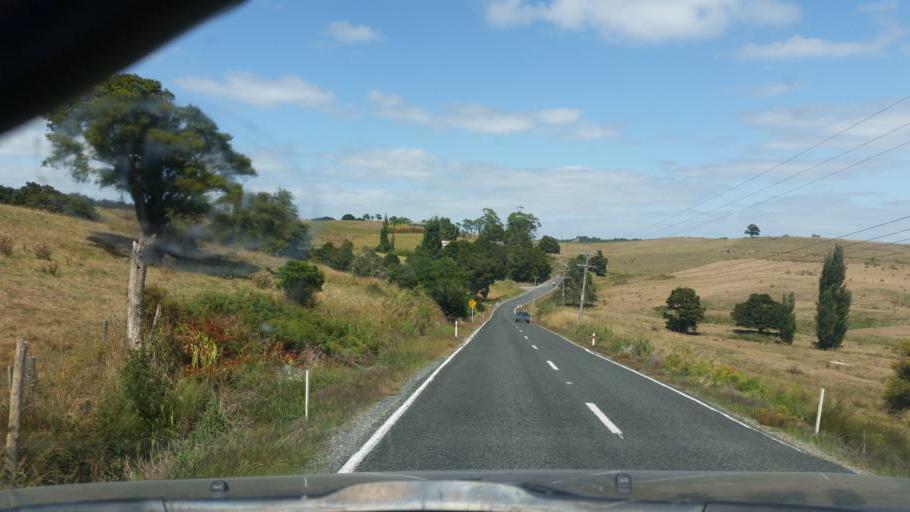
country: NZ
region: Northland
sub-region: Whangarei
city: Ruakaka
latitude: -36.0138
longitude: 174.2901
